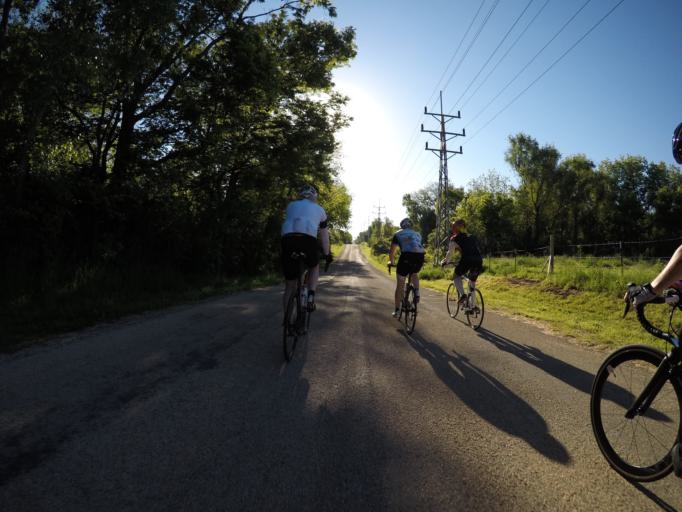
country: US
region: Kansas
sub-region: Shawnee County
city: Topeka
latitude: 39.0516
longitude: -95.6159
